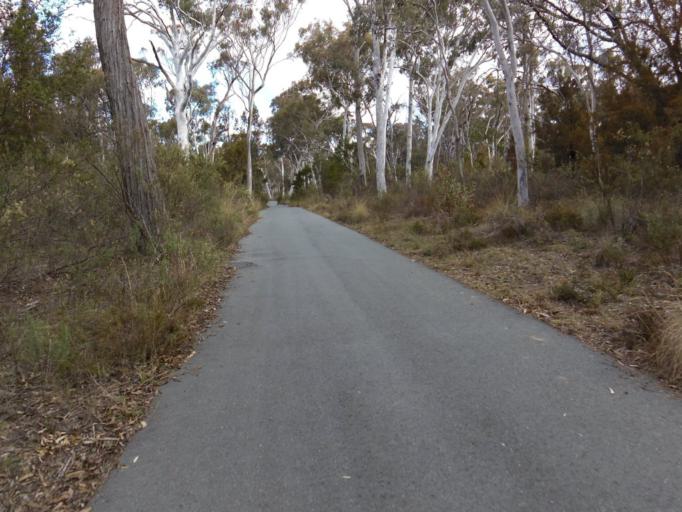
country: AU
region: Australian Capital Territory
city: Macquarie
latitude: -35.2498
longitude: 149.0933
